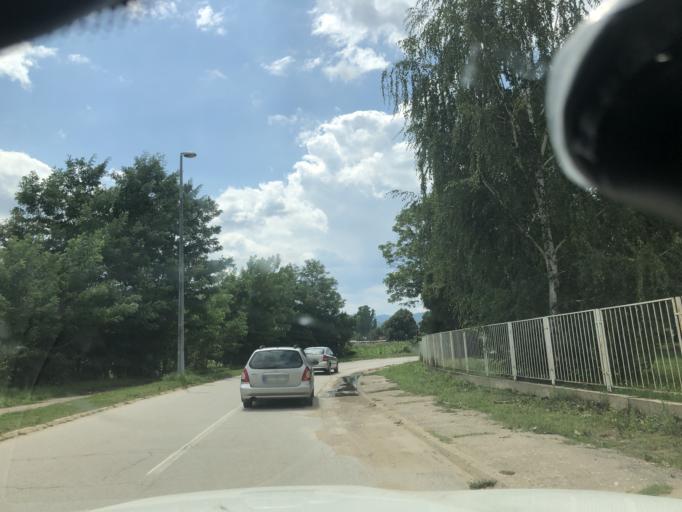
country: RS
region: Central Serbia
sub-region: Jablanicki Okrug
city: Medvega
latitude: 42.8419
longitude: 21.5871
